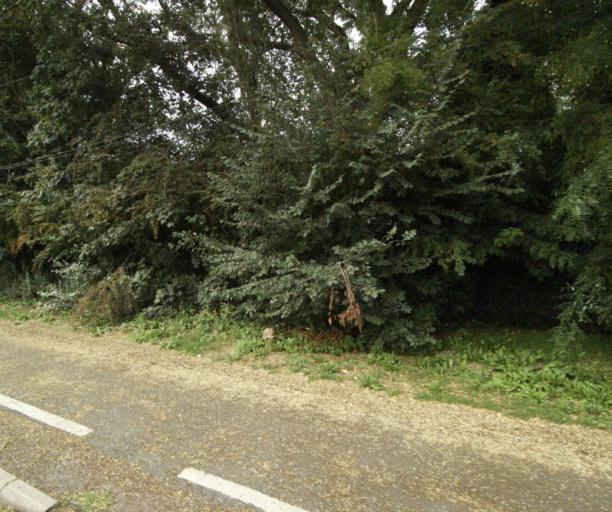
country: FR
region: Nord-Pas-de-Calais
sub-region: Departement du Nord
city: Villeneuve-d'Ascq
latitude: 50.6088
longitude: 3.1709
